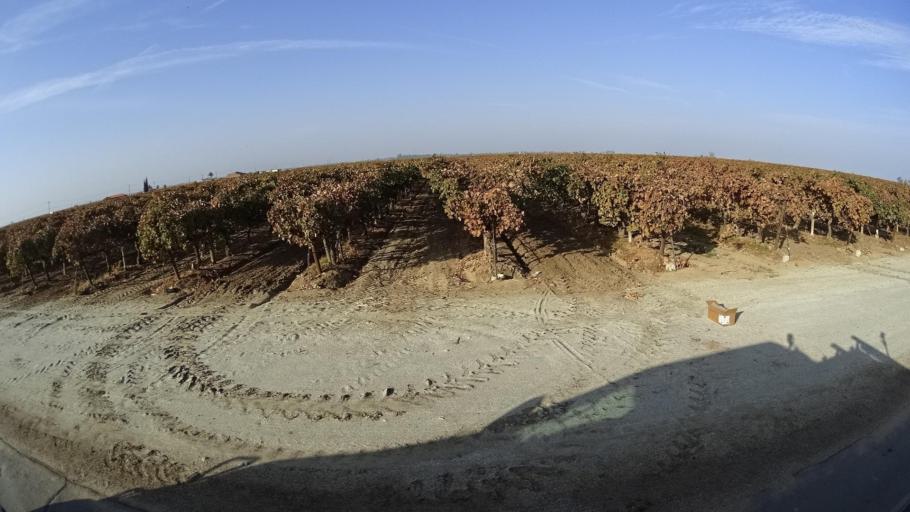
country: US
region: California
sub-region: Kern County
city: McFarland
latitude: 35.6772
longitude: -119.1871
